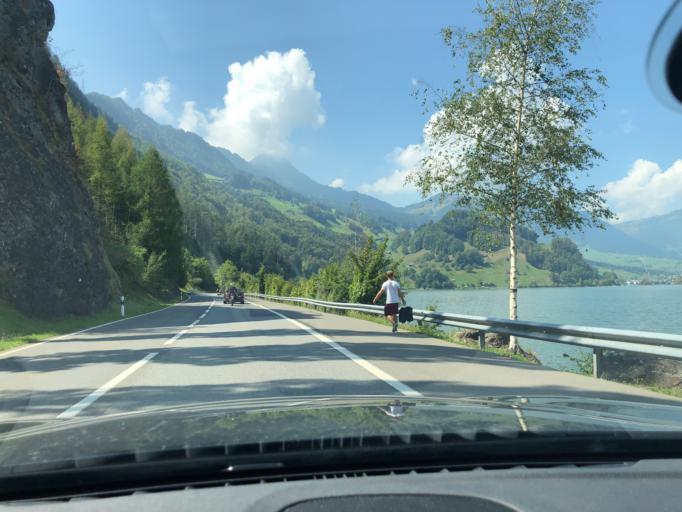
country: CH
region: Schwyz
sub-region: Bezirk Schwyz
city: Steinen
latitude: 47.0289
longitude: 8.6201
